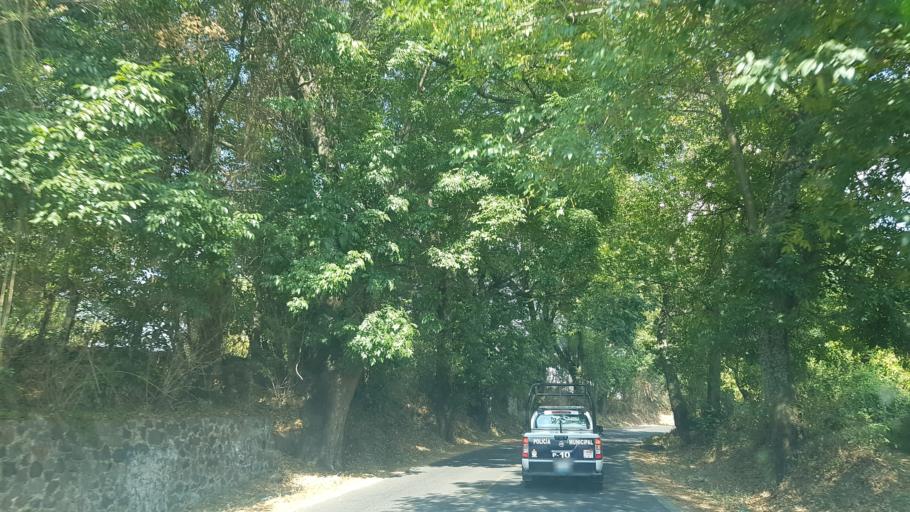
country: MX
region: Puebla
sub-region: Atlixco
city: Colonia Agricola de Ocotepec (Colonia San Jose)
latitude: 18.9218
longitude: -98.5397
